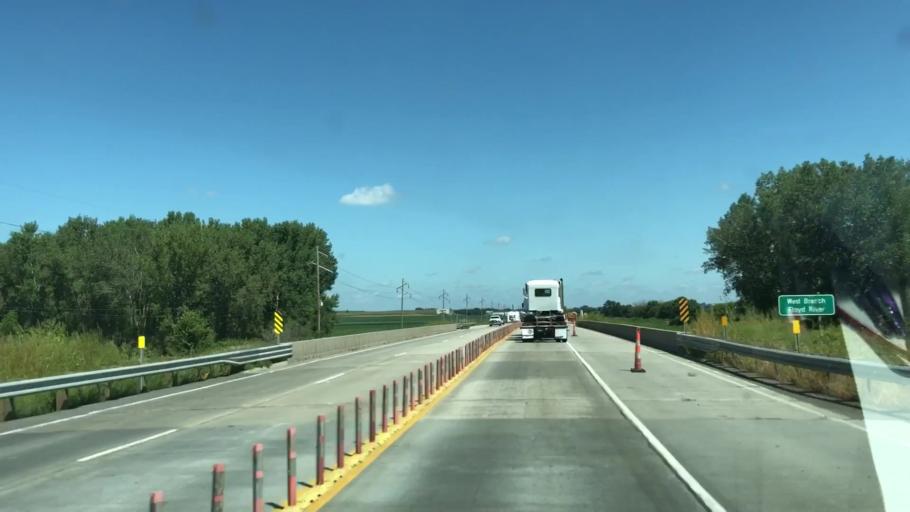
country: US
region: Iowa
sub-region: Plymouth County
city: Le Mars
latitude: 42.7241
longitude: -96.2420
